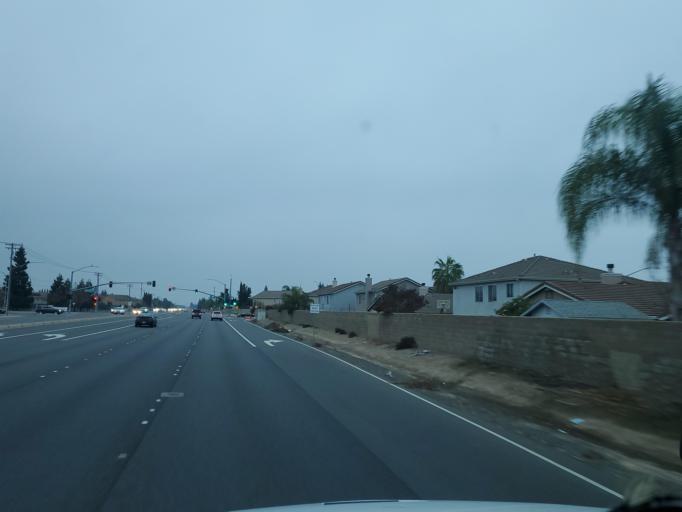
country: US
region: California
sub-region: Stanislaus County
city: Del Rio
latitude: 37.7006
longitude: -121.0301
